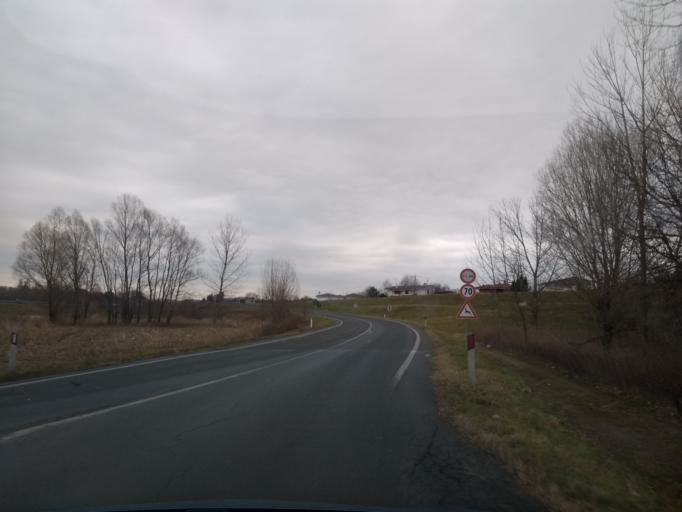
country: IT
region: Piedmont
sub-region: Provincia di Torino
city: Salerano Canavese
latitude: 45.4630
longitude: 7.8472
